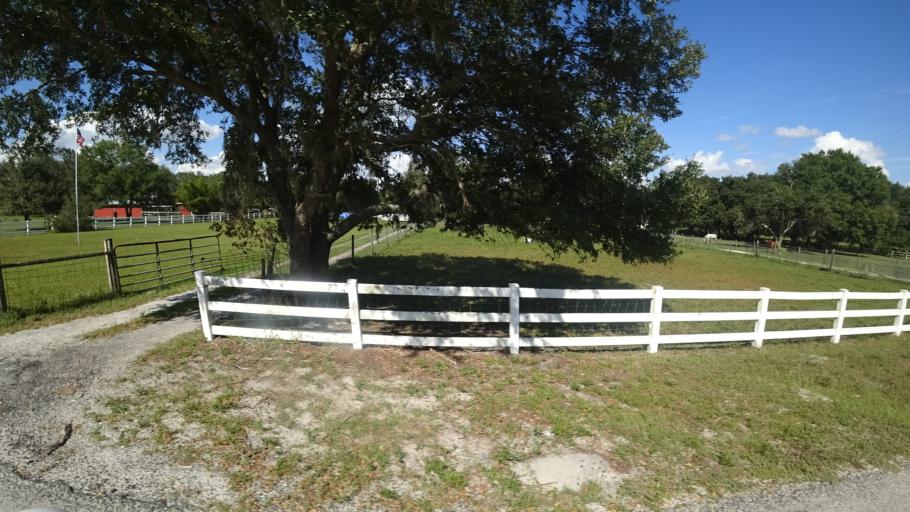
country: US
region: Florida
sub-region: Sarasota County
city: The Meadows
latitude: 27.4671
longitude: -82.2927
